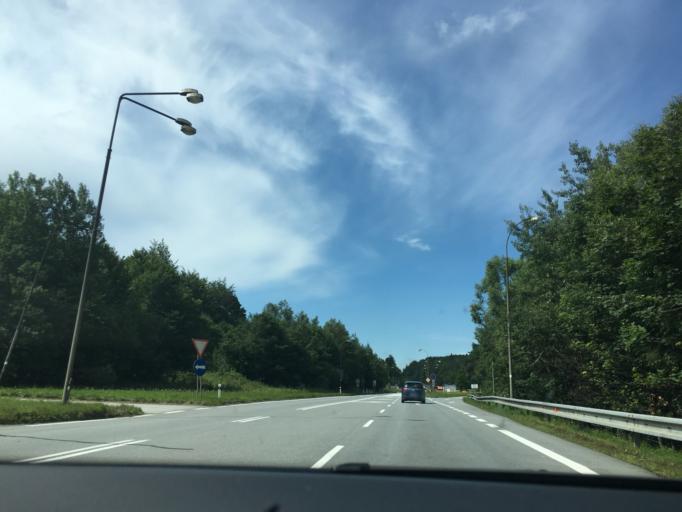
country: PL
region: Subcarpathian Voivodeship
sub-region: Powiat krosnienski
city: Jasliska
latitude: 49.4094
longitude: 21.7010
